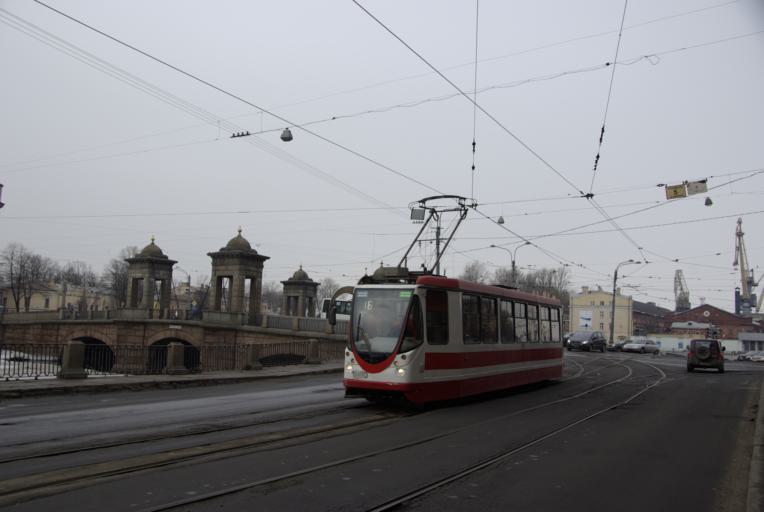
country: RU
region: St.-Petersburg
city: Admiralteisky
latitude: 59.9168
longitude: 30.2807
